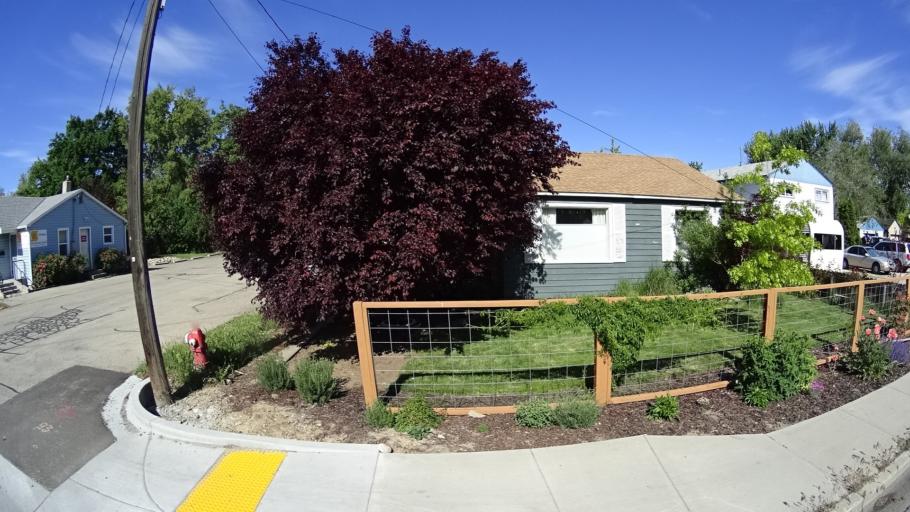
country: US
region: Idaho
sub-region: Ada County
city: Garden City
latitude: 43.5986
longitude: -116.2437
